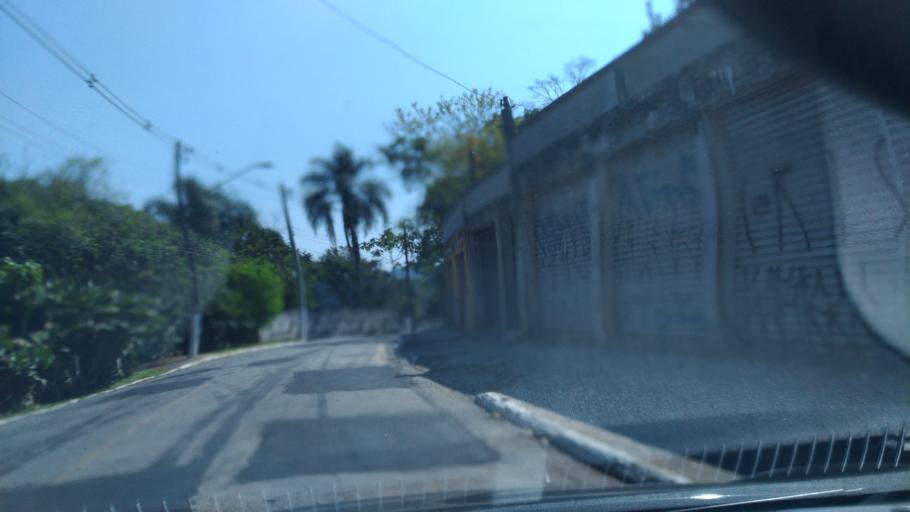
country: BR
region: Sao Paulo
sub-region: Sao Bernardo Do Campo
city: Sao Bernardo do Campo
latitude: -23.7756
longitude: -46.5227
